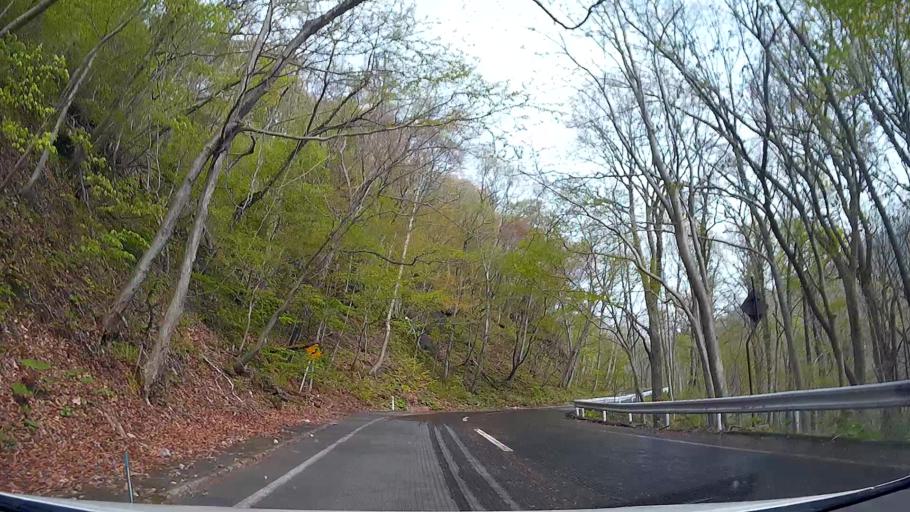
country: JP
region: Akita
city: Hanawa
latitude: 40.4258
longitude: 140.9074
